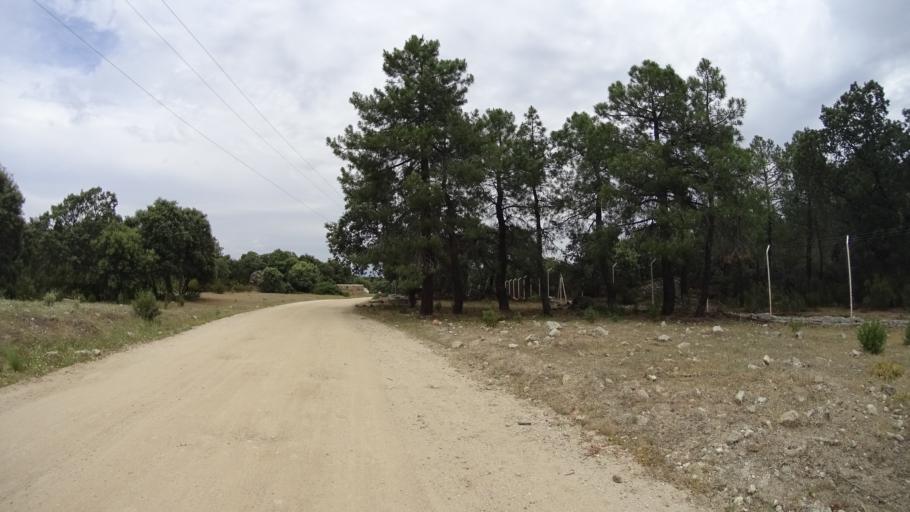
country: ES
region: Madrid
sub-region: Provincia de Madrid
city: Colmenarejo
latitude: 40.5585
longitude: -4.0363
